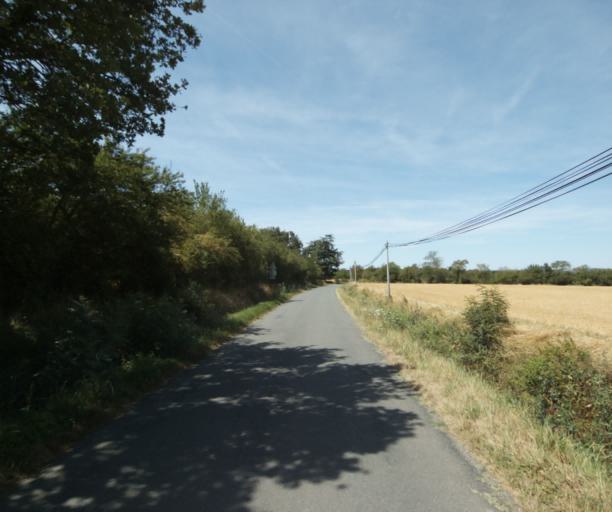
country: FR
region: Midi-Pyrenees
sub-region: Departement de la Haute-Garonne
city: Revel
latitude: 43.4967
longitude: 2.0037
